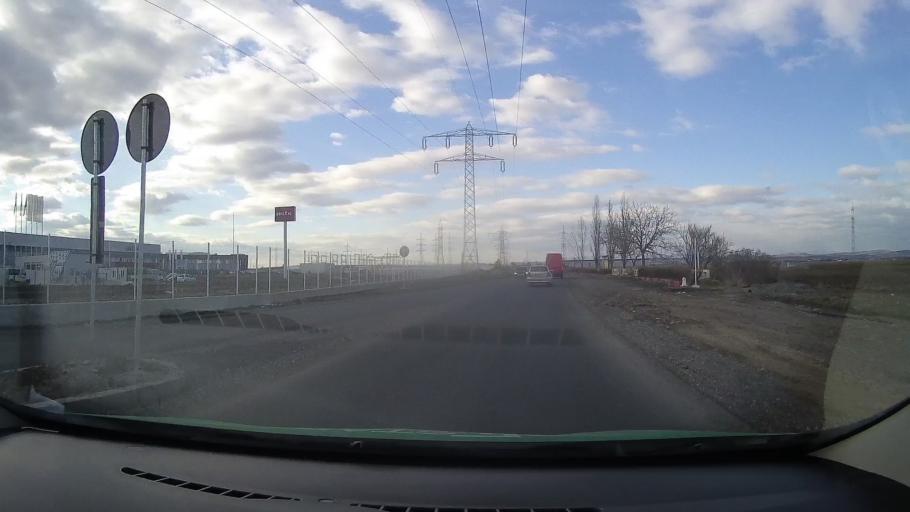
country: RO
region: Dambovita
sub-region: Comuna Comisani
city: Lazuri
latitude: 44.8758
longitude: 25.5193
